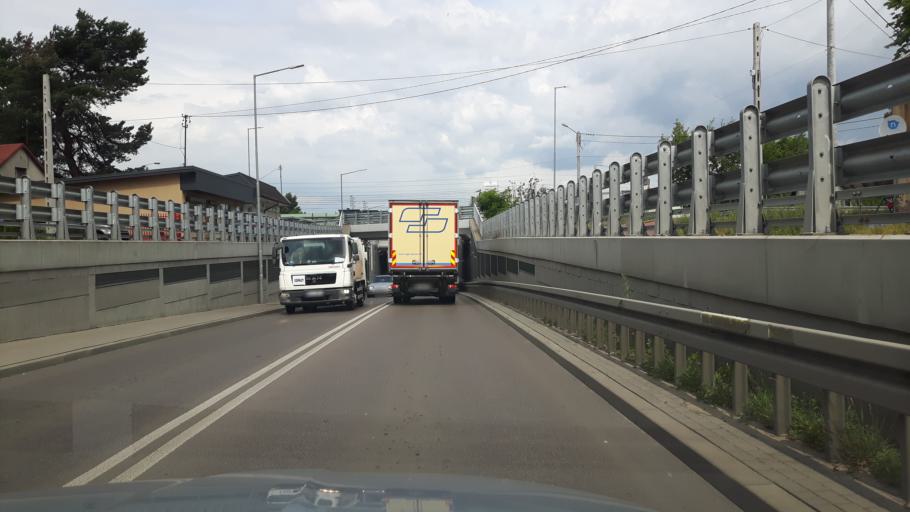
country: PL
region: Masovian Voivodeship
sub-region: Powiat wolominski
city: Nowe Lipiny
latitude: 52.3541
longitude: 21.2583
